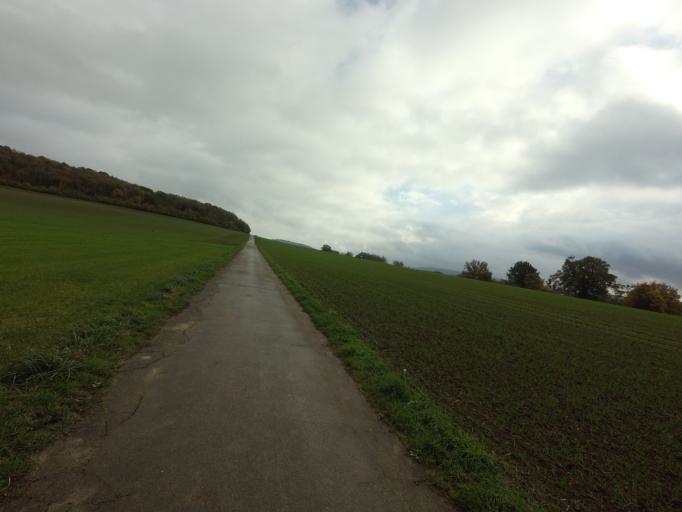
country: NL
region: Limburg
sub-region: Gemeente Simpelveld
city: Simpelveld
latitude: 50.7974
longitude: 5.9803
